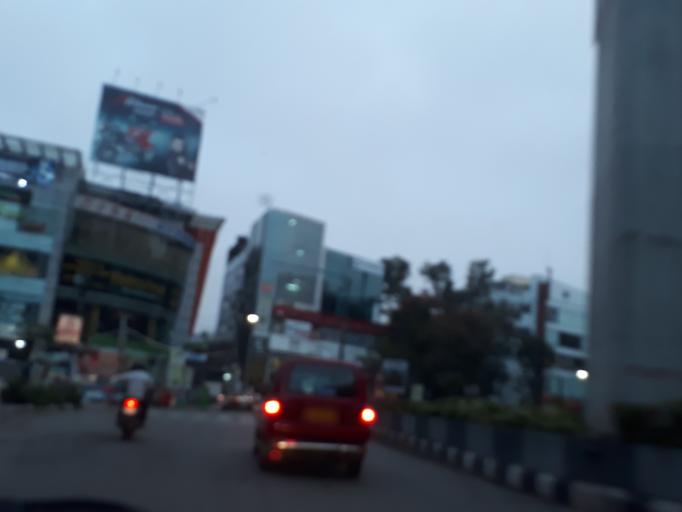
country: IN
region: Telangana
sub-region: Rangareddi
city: Kukatpalli
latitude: 17.4313
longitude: 78.4073
